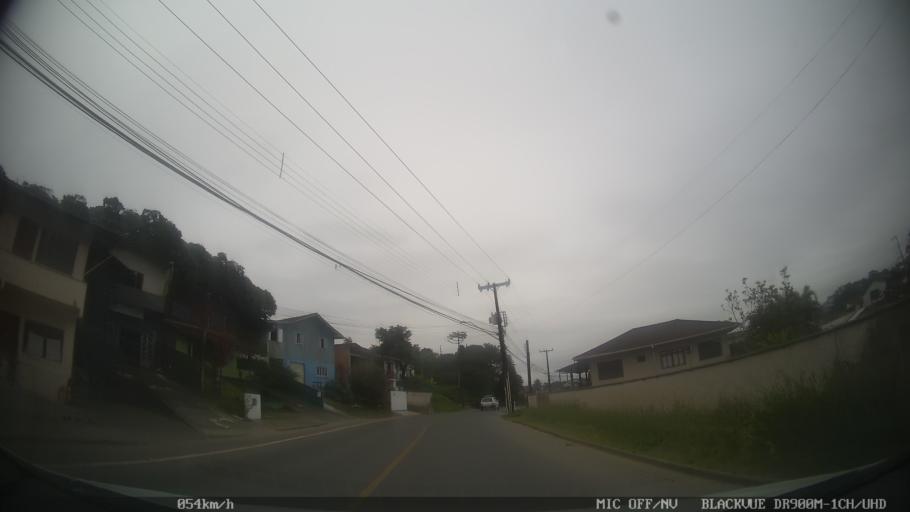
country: BR
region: Santa Catarina
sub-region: Joinville
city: Joinville
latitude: -26.3558
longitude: -48.8199
